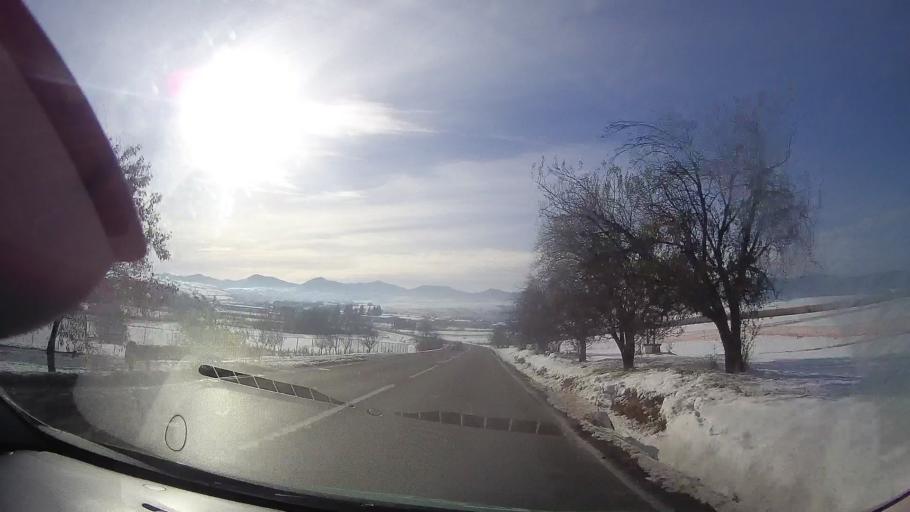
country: RO
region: Neamt
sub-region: Comuna Baltatesti
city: Valea Seaca
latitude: 47.1472
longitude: 26.3222
